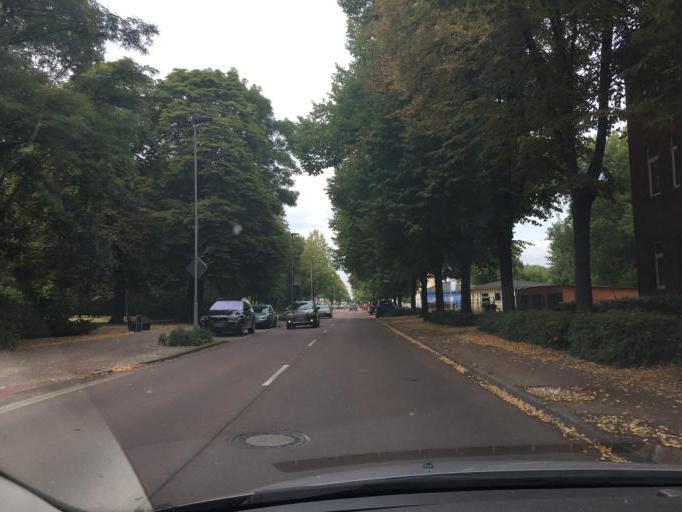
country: DE
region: Saxony-Anhalt
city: Merseburg
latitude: 51.3638
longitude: 11.9910
